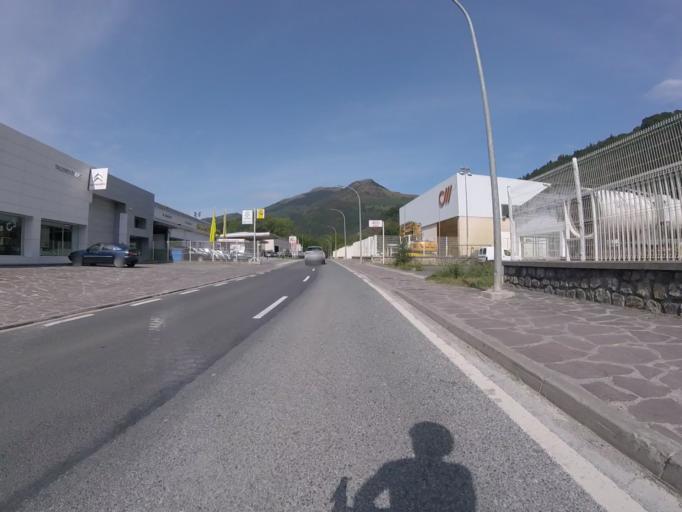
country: ES
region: Navarre
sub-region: Provincia de Navarra
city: Elgorriaga
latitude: 43.1359
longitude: -1.6795
